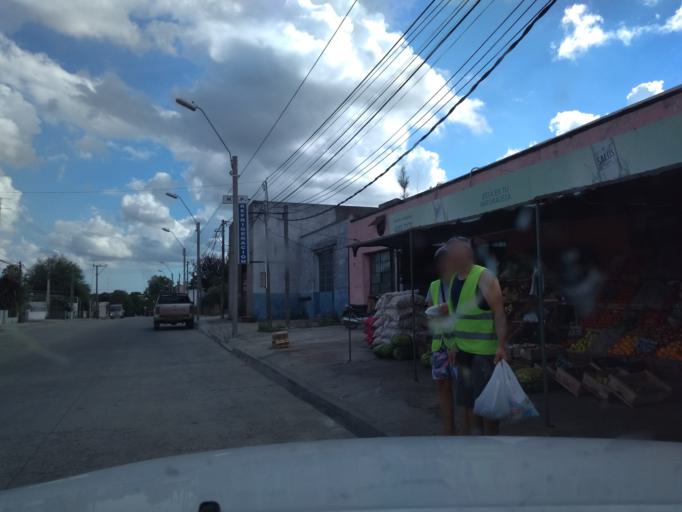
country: UY
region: Florida
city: Florida
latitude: -34.0890
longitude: -56.2147
